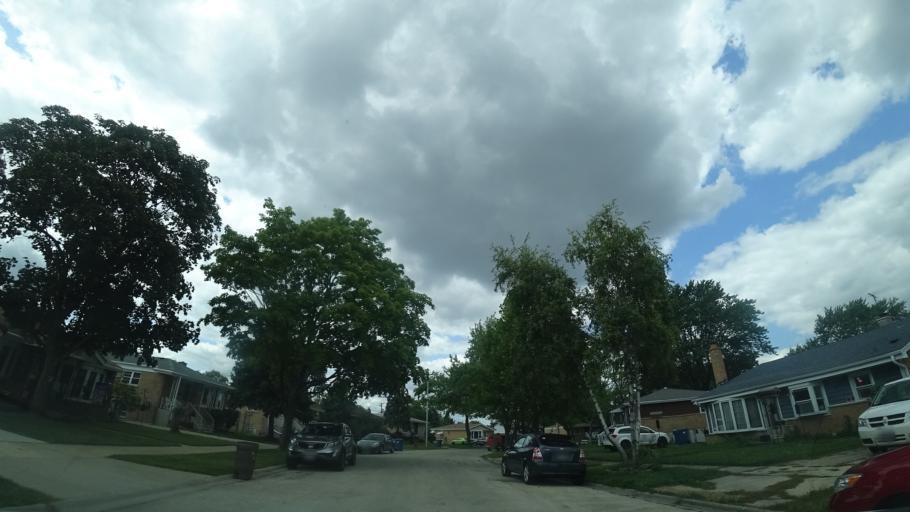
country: US
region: Illinois
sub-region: Cook County
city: Alsip
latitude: 41.6817
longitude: -87.7277
